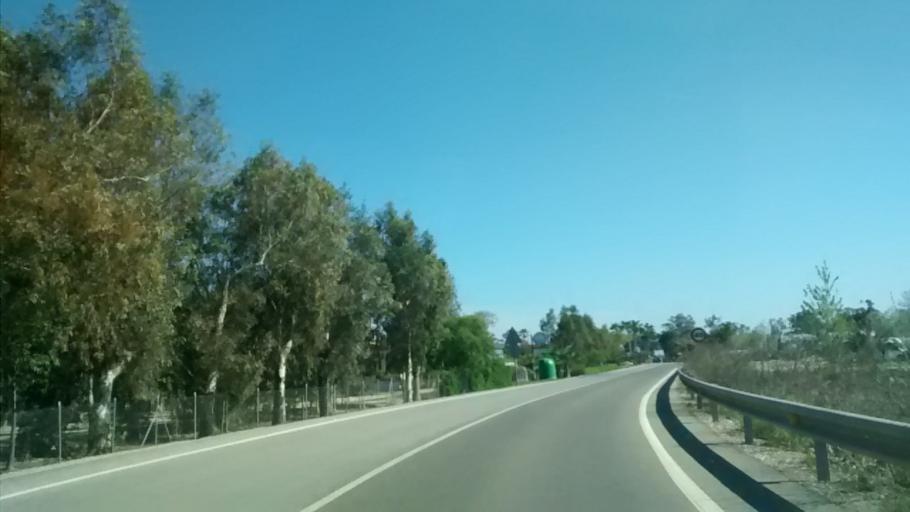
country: ES
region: Catalonia
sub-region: Provincia de Tarragona
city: Deltebre
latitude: 40.7151
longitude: 0.8333
